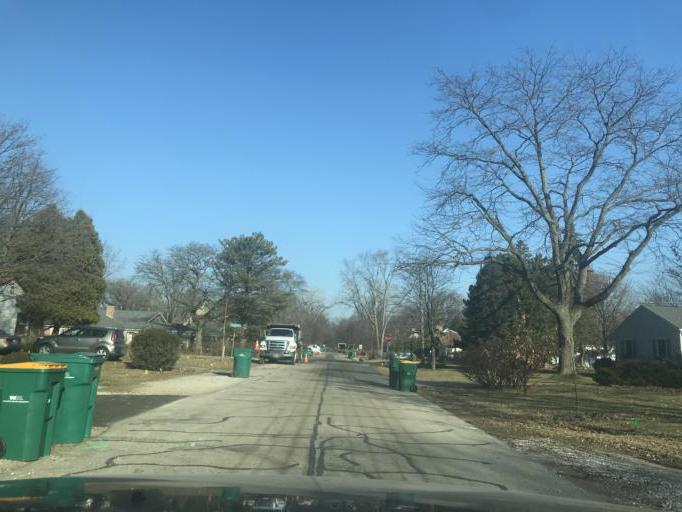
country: US
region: Illinois
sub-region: Cook County
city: Northfield
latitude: 42.0972
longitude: -87.7625
